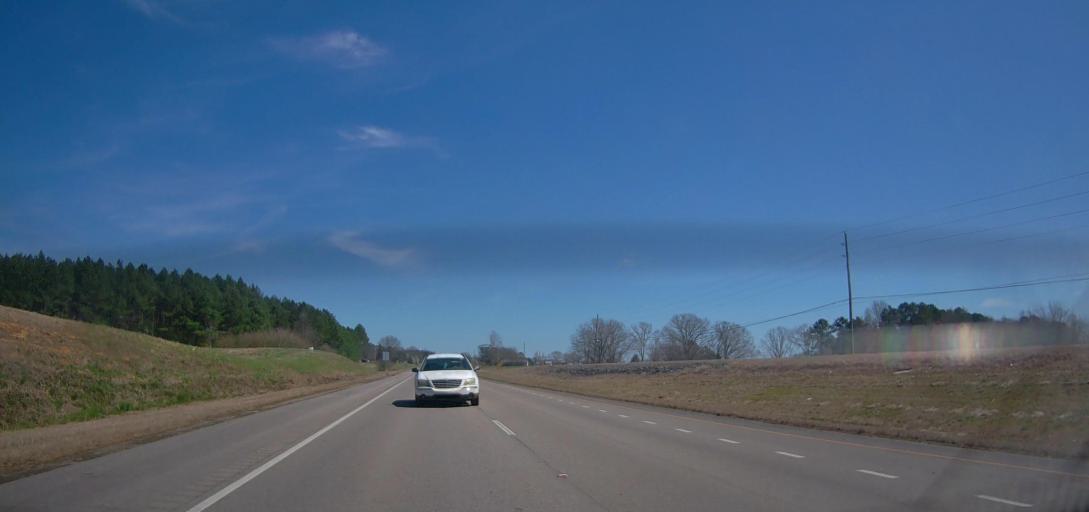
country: US
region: Alabama
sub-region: Cullman County
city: Hanceville
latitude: 34.1758
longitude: -86.7182
